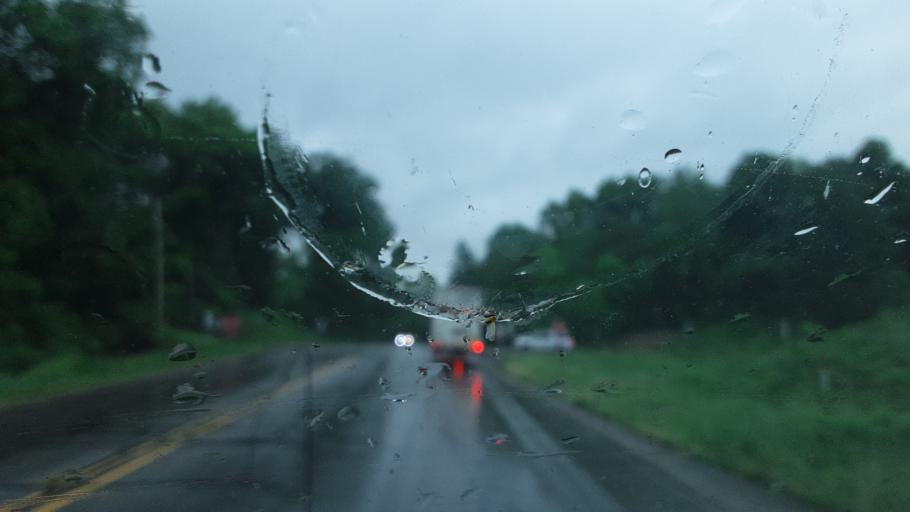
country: US
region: Indiana
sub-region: Steuben County
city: Fremont
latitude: 41.7473
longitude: -85.0005
